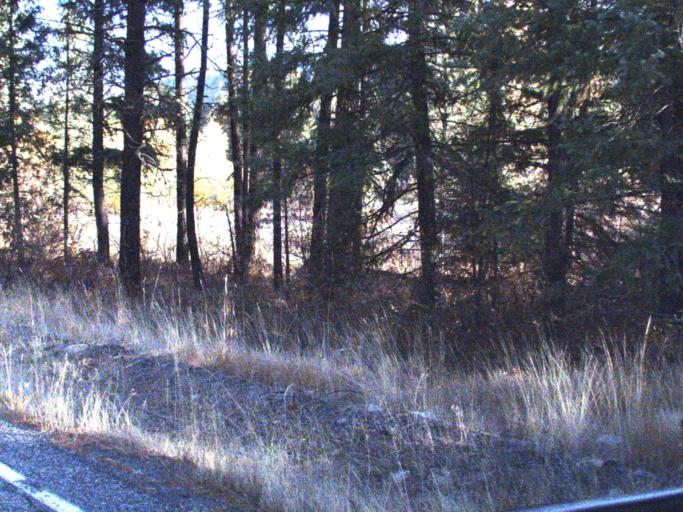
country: US
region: Washington
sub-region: Ferry County
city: Republic
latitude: 48.3819
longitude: -118.7483
